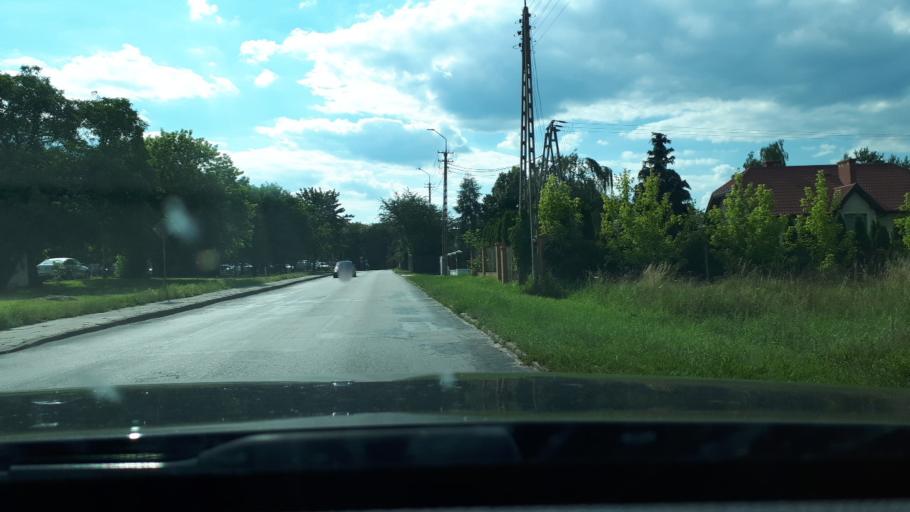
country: PL
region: Masovian Voivodeship
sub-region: Powiat grojecki
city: Warka
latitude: 51.7911
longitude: 21.1874
